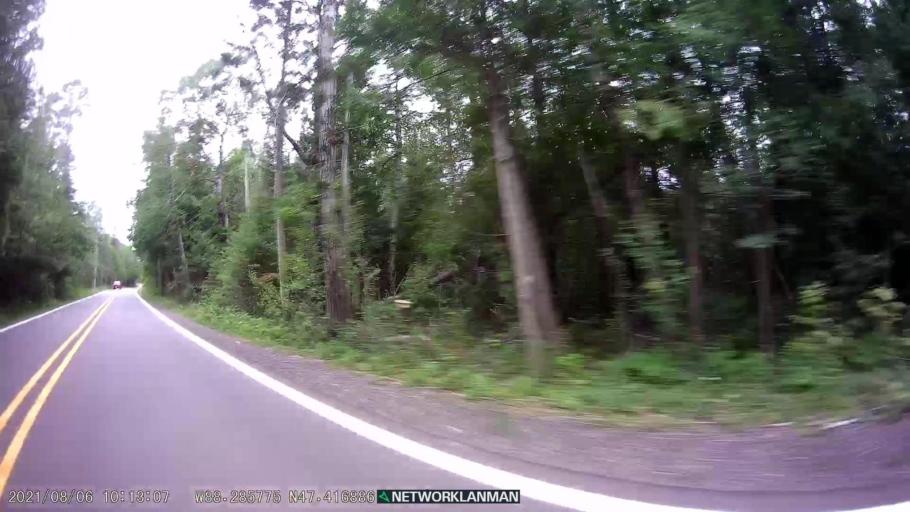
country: US
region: Michigan
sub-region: Keweenaw County
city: Eagle River
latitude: 47.4169
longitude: -88.2866
